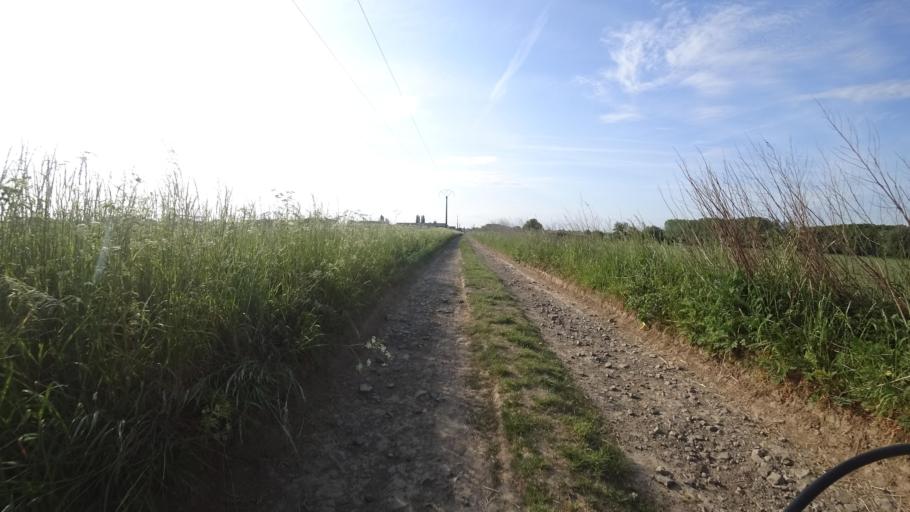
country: BE
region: Wallonia
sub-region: Province de Namur
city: Gembloux
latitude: 50.5818
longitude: 4.6977
